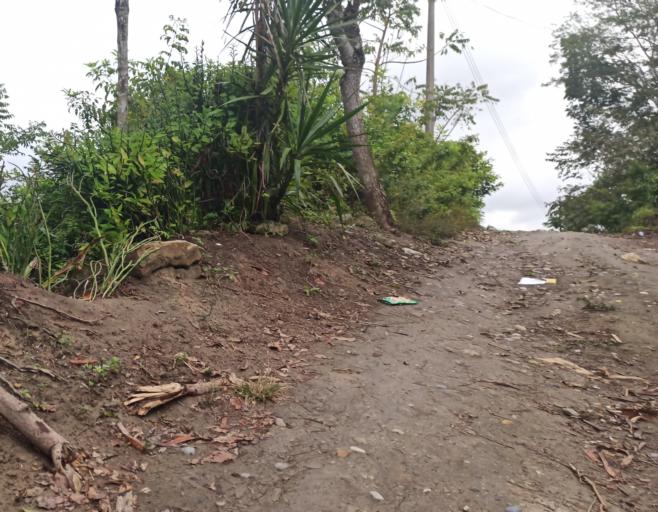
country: MX
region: Puebla
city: Espinal
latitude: 20.2911
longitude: -97.3968
